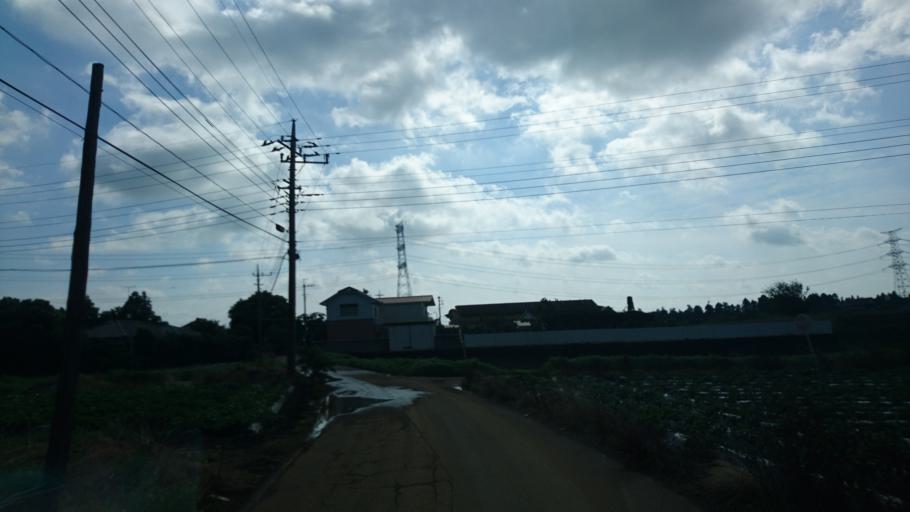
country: JP
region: Chiba
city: Sawara
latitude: 35.8501
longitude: 140.4726
